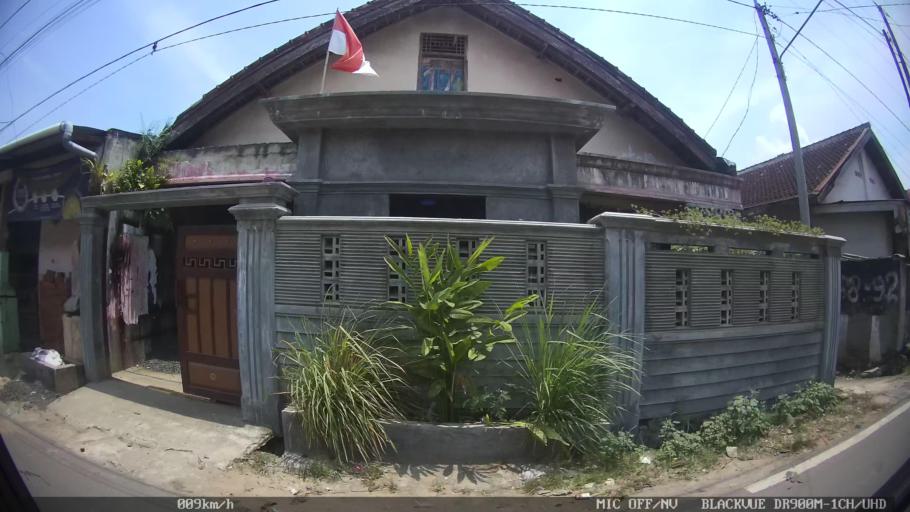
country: ID
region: Lampung
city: Bandarlampung
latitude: -5.4402
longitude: 105.2408
